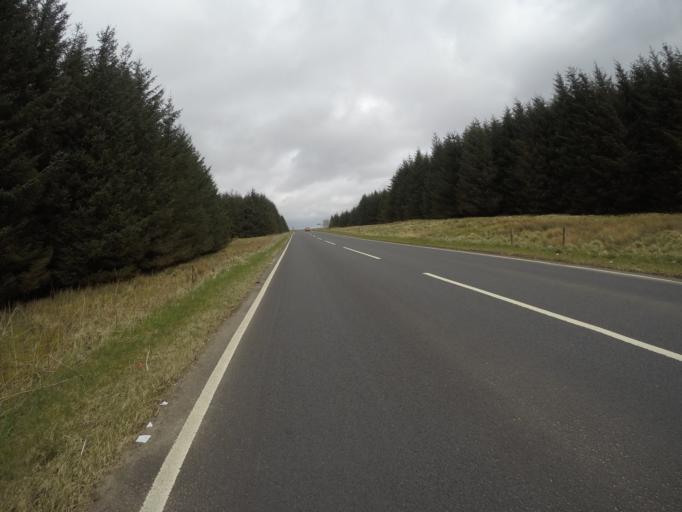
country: GB
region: Scotland
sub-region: East Renfrewshire
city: Newton Mearns
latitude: 55.7044
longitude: -4.3696
